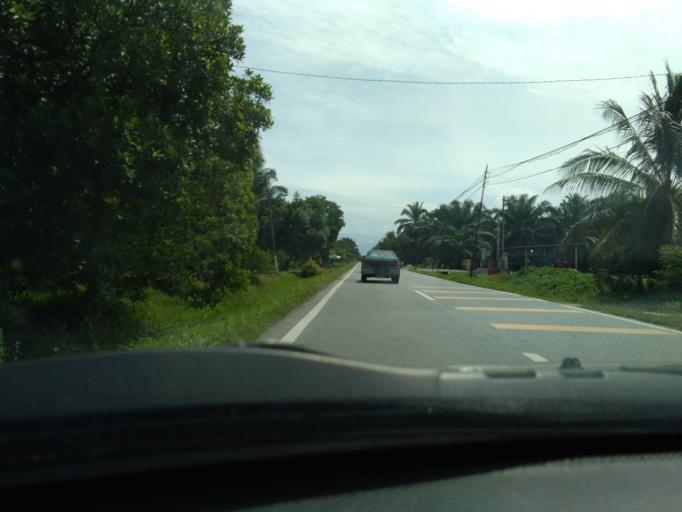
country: MY
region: Perak
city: Bagan Serai
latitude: 5.0367
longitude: 100.5684
